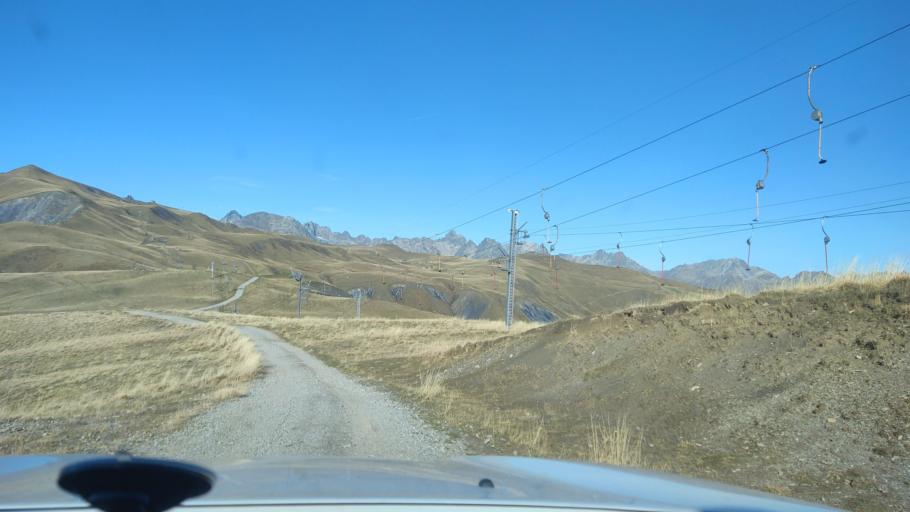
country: FR
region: Rhone-Alpes
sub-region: Departement de la Savoie
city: Saint-Jean-de-Maurienne
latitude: 45.2365
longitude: 6.2409
